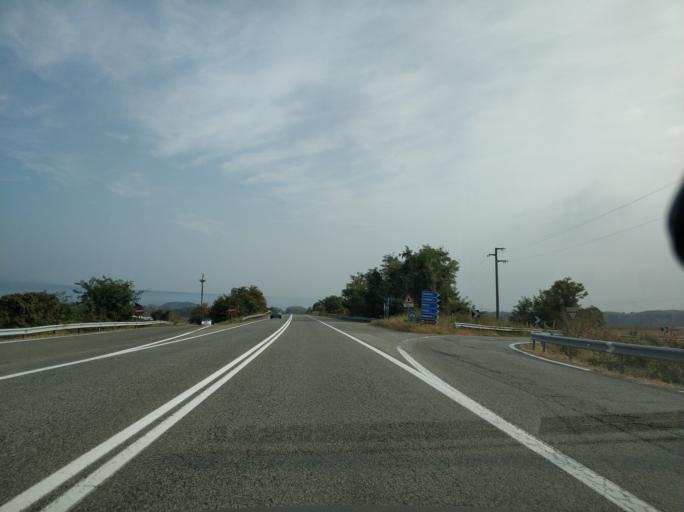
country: IT
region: Piedmont
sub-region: Provincia di Torino
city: Parella
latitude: 45.4241
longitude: 7.7970
